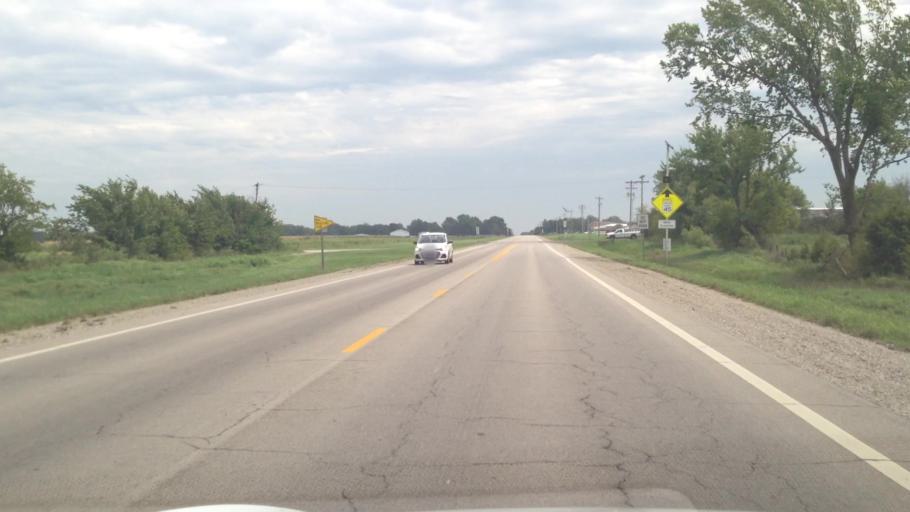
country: US
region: Kansas
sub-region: Crawford County
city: Girard
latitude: 37.5140
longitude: -94.8718
